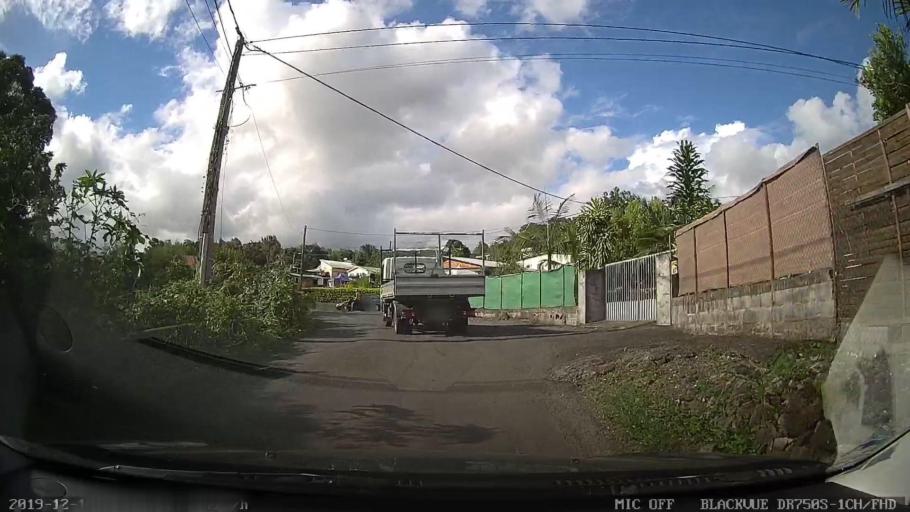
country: RE
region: Reunion
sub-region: Reunion
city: Le Tampon
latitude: -21.2531
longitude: 55.5110
